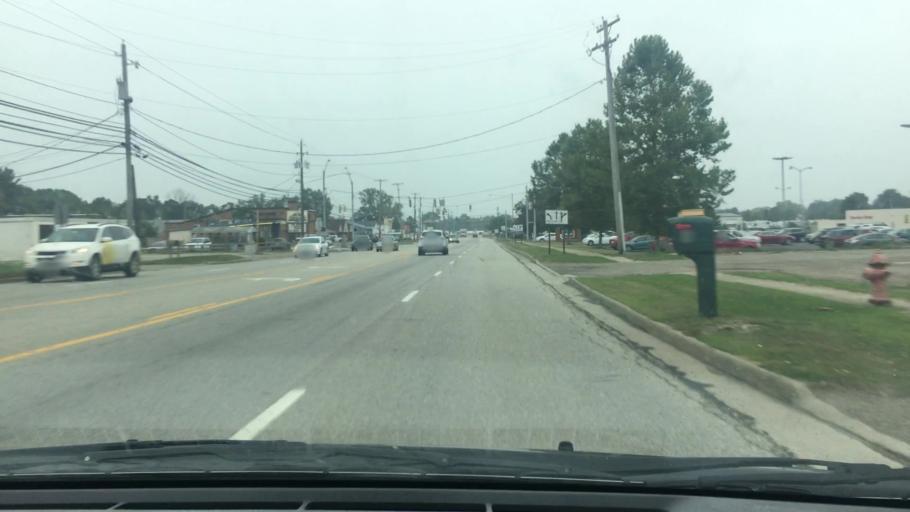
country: US
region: Ohio
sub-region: Portage County
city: Streetsboro
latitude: 41.2383
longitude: -81.3387
